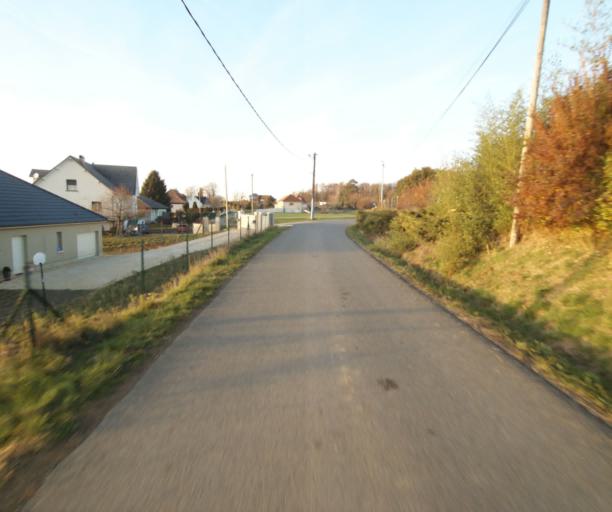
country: FR
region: Limousin
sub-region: Departement de la Correze
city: Laguenne
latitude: 45.2284
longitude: 1.8253
